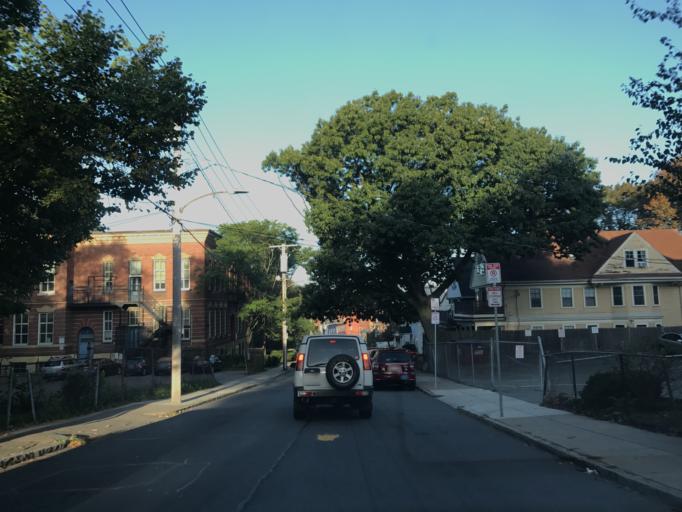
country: US
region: Massachusetts
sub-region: Suffolk County
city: Jamaica Plain
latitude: 42.3089
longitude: -71.1026
